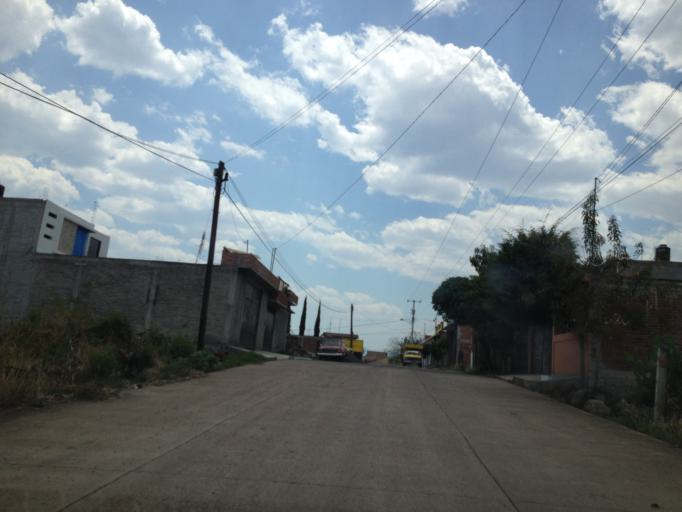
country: MX
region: Michoacan
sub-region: Morelia
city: San Antonio
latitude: 19.7085
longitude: -101.2470
